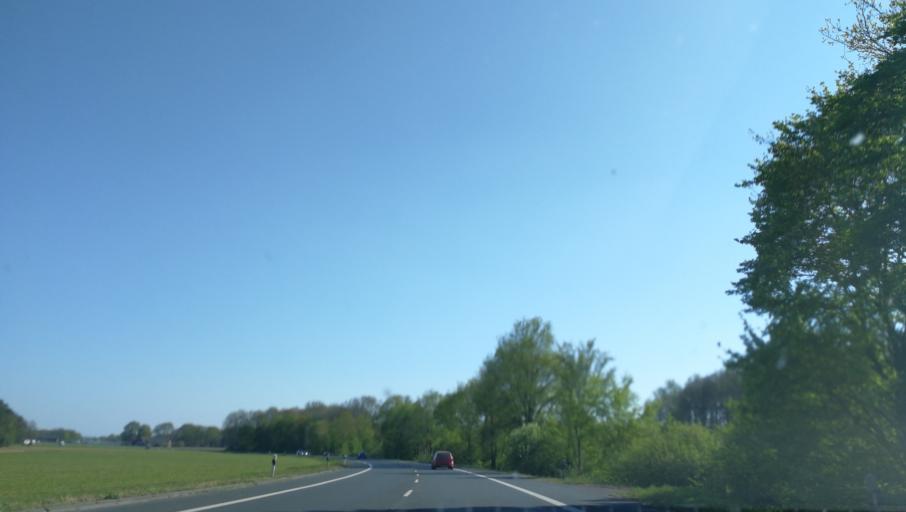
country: DE
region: North Rhine-Westphalia
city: Emsdetten
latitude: 52.2109
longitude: 7.5055
